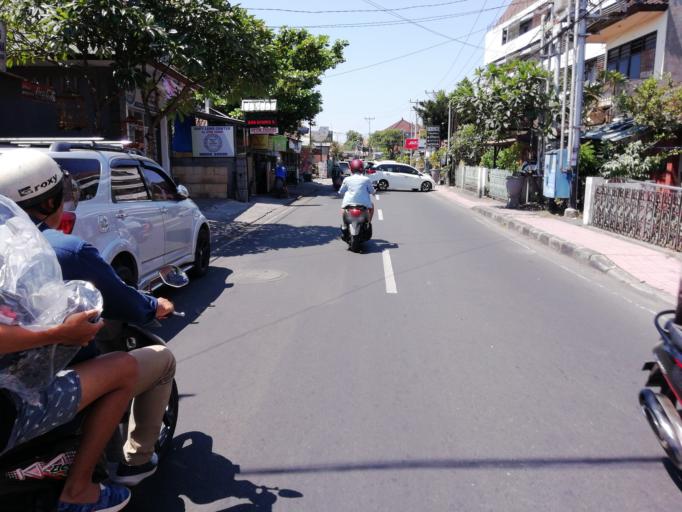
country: ID
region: Bali
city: Denpasar
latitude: -8.6762
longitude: 115.2076
